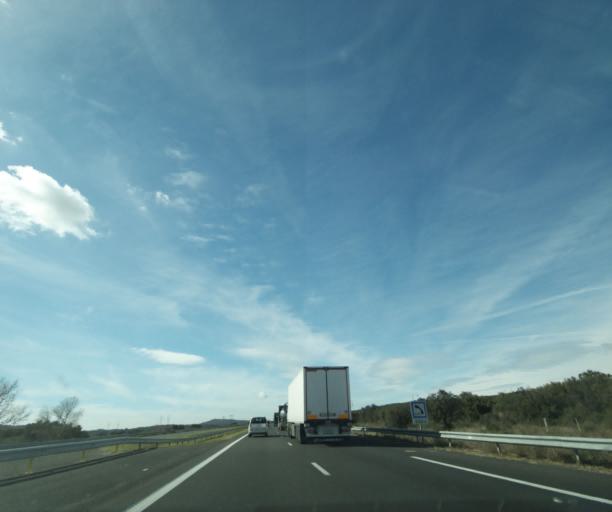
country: FR
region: Languedoc-Roussillon
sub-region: Departement du Gard
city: Rochefort-du-Gard
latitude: 43.9884
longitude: 4.6823
